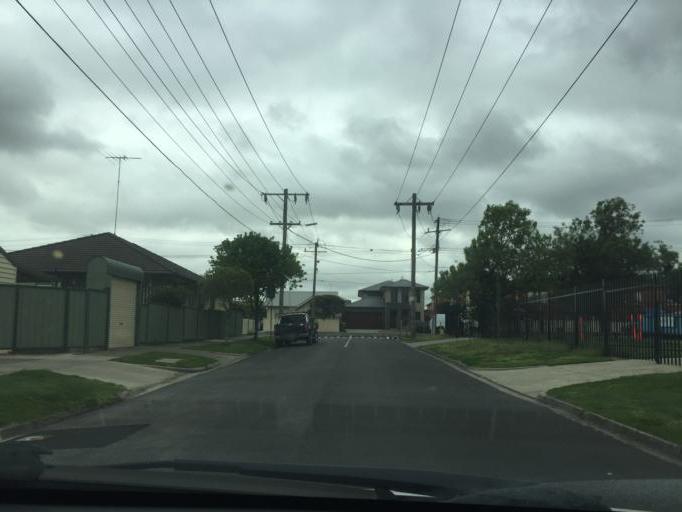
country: AU
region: Victoria
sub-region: Maribyrnong
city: Kingsville
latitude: -37.8123
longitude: 144.8734
